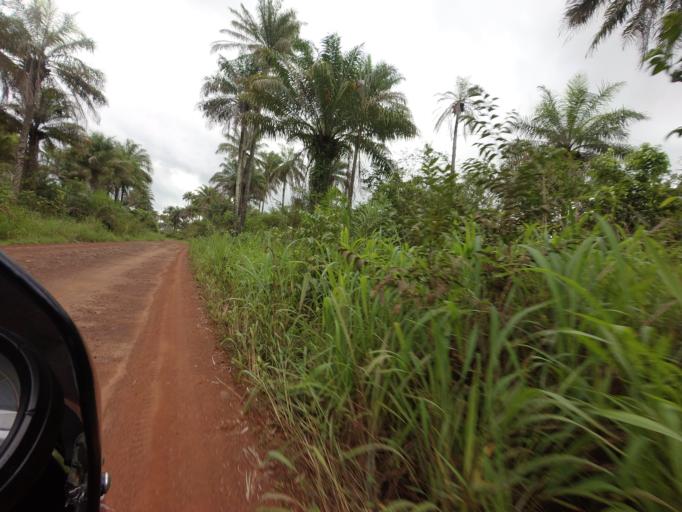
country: SL
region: Northern Province
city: Kambia
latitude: 9.1031
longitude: -12.9910
